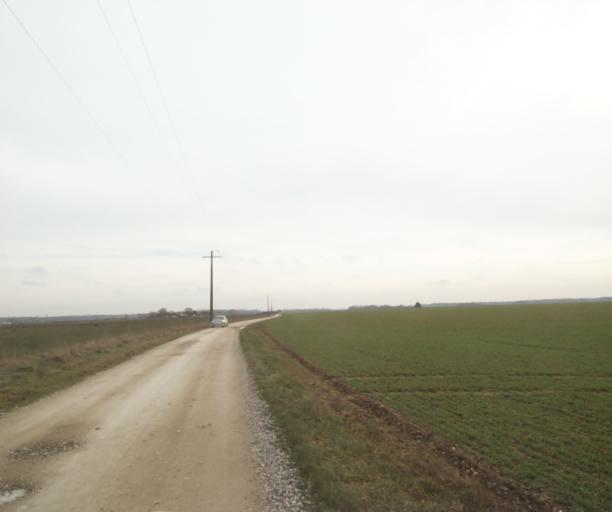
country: FR
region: Champagne-Ardenne
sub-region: Departement de la Haute-Marne
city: Villiers-en-Lieu
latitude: 48.6762
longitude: 4.8655
